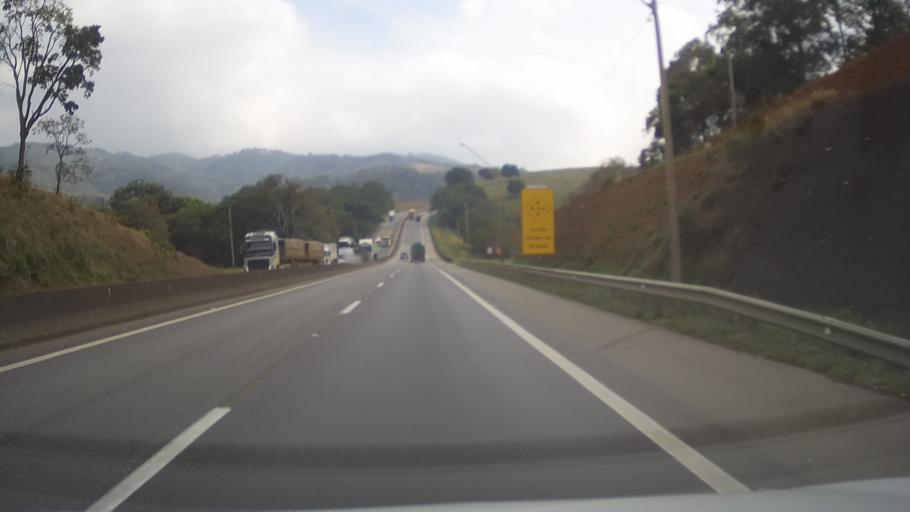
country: BR
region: Minas Gerais
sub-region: Extrema
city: Extrema
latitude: -22.8890
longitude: -46.4124
